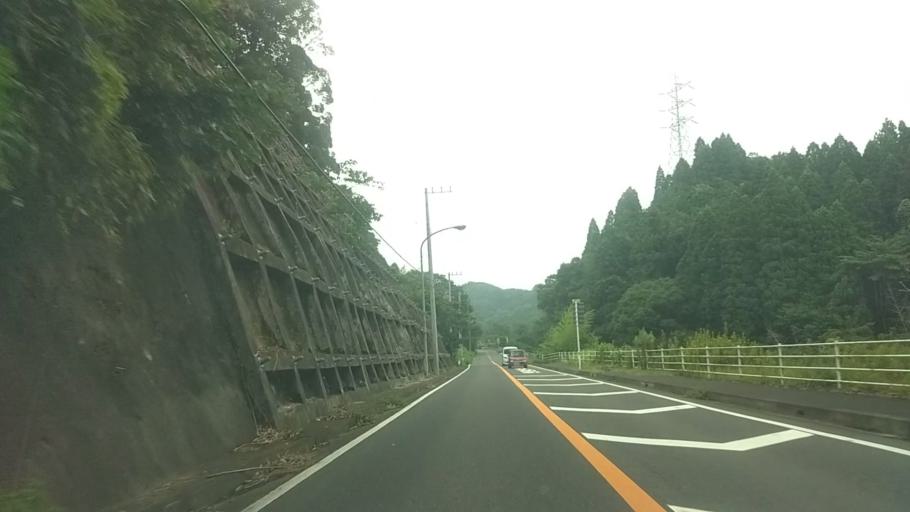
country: JP
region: Chiba
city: Kawaguchi
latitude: 35.2522
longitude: 140.0706
